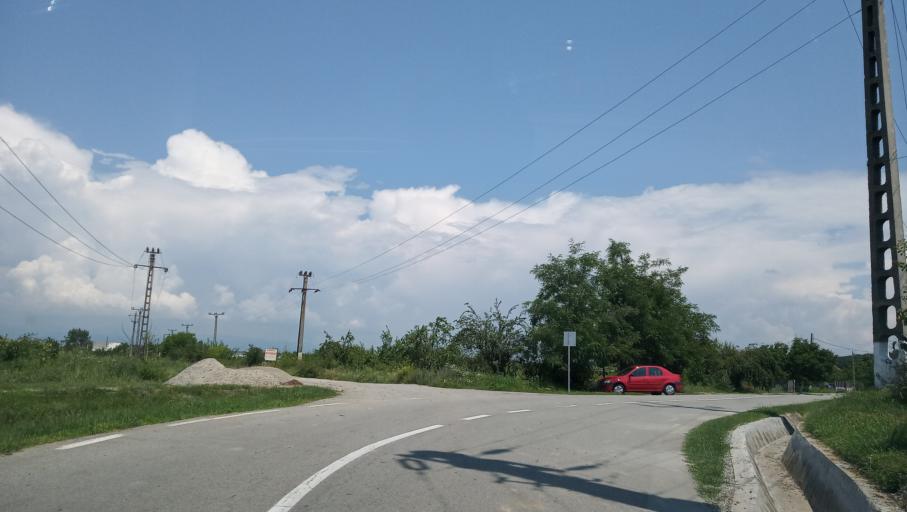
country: RO
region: Gorj
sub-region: Comuna Turcinesti
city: Turcinesti
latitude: 45.0459
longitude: 23.3433
